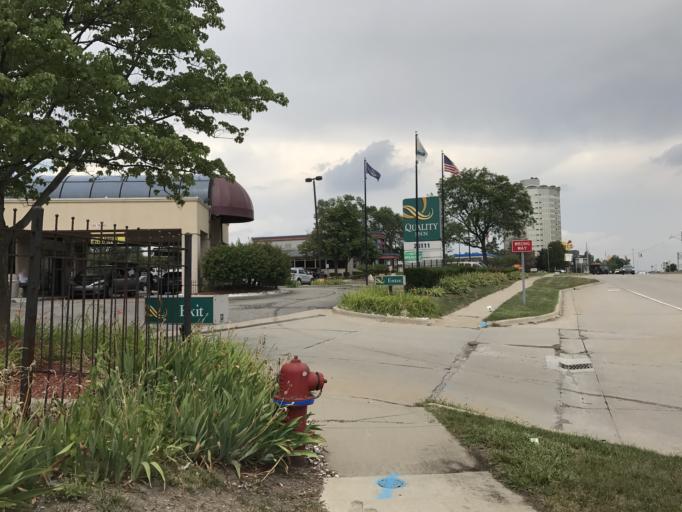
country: US
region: Michigan
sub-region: Oakland County
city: Bingham Farms
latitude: 42.4809
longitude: -83.2859
